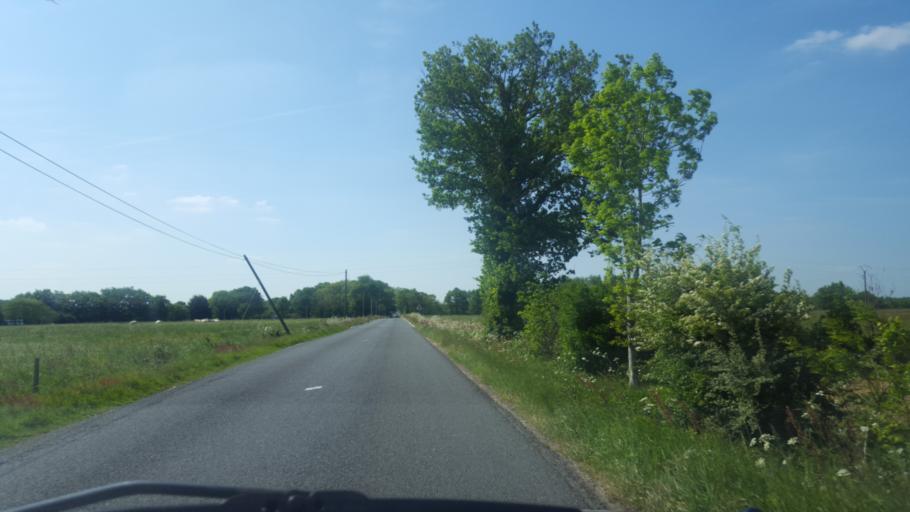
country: FR
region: Pays de la Loire
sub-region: Departement de la Loire-Atlantique
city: Saint-Philbert-de-Grand-Lieu
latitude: 47.0384
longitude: -1.5973
